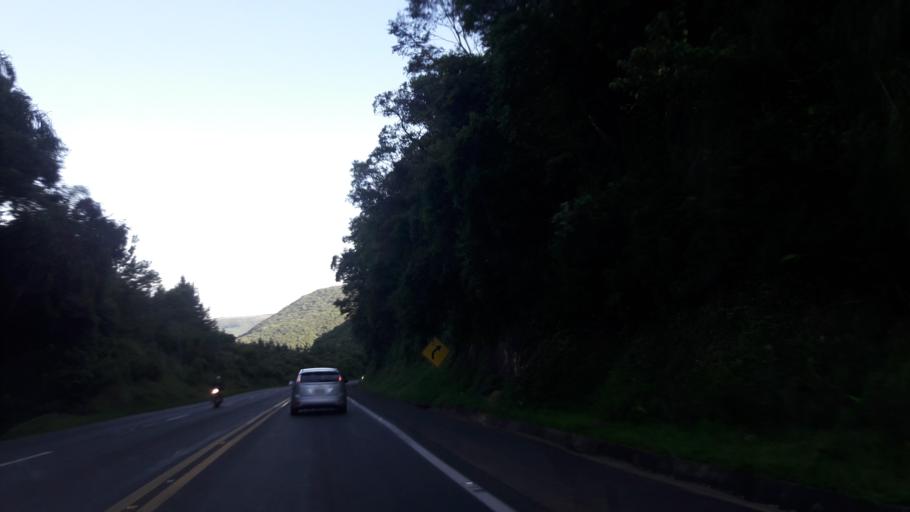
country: BR
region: Parana
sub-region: Prudentopolis
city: Prudentopolis
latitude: -25.3124
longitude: -51.2039
